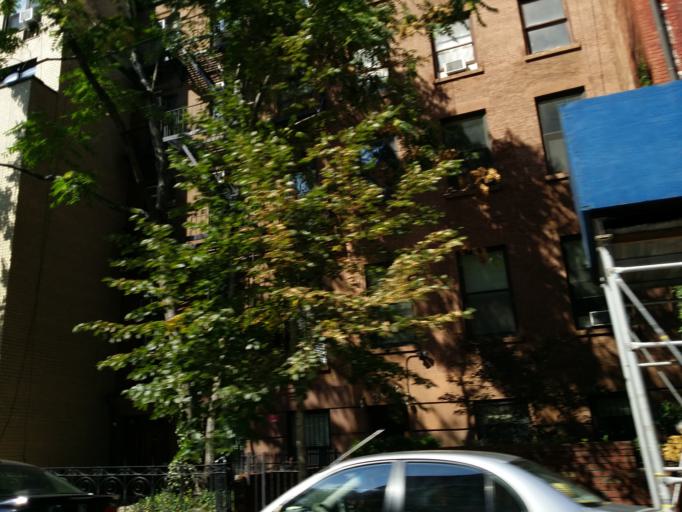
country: US
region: New Jersey
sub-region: Hudson County
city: Weehawken
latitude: 40.7494
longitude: -73.9962
